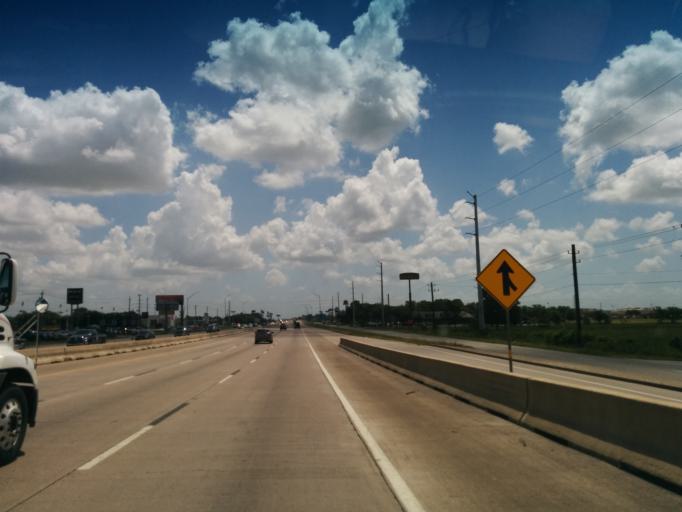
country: US
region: Texas
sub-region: Harris County
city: Highlands
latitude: 29.8026
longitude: -94.9941
